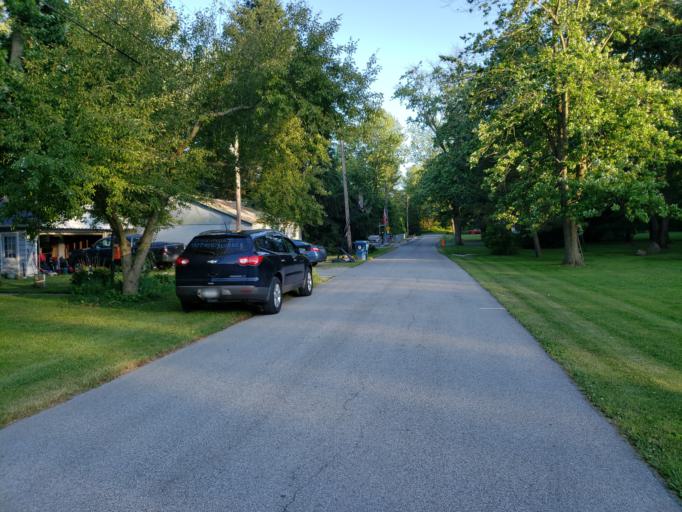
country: US
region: Indiana
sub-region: Lake County
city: Cedar Lake
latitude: 41.3361
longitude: -87.4324
